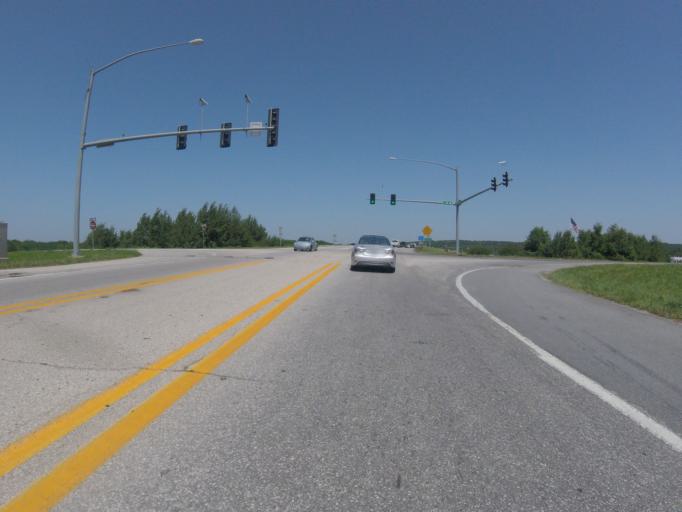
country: US
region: Arkansas
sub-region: Washington County
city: Johnson
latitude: 36.1044
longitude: -94.1789
